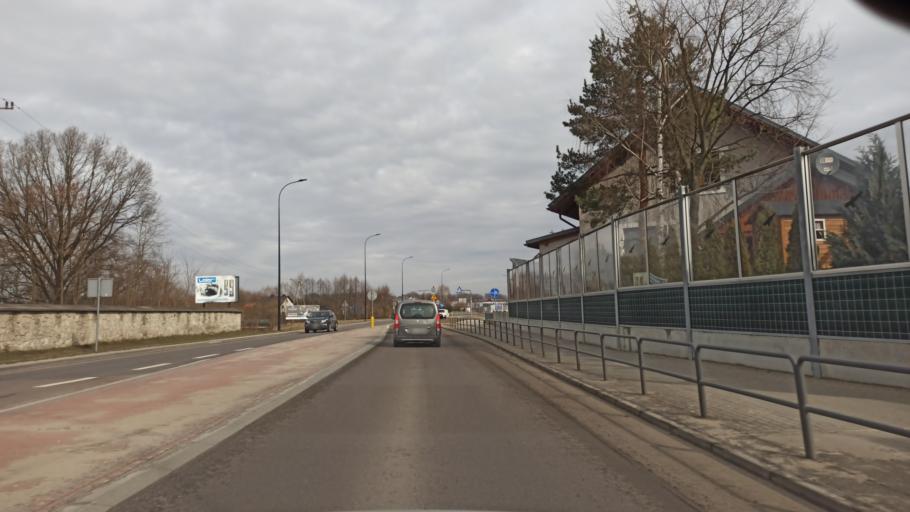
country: PL
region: Lublin Voivodeship
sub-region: Powiat bilgorajski
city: Bilgoraj
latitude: 50.5253
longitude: 22.7083
